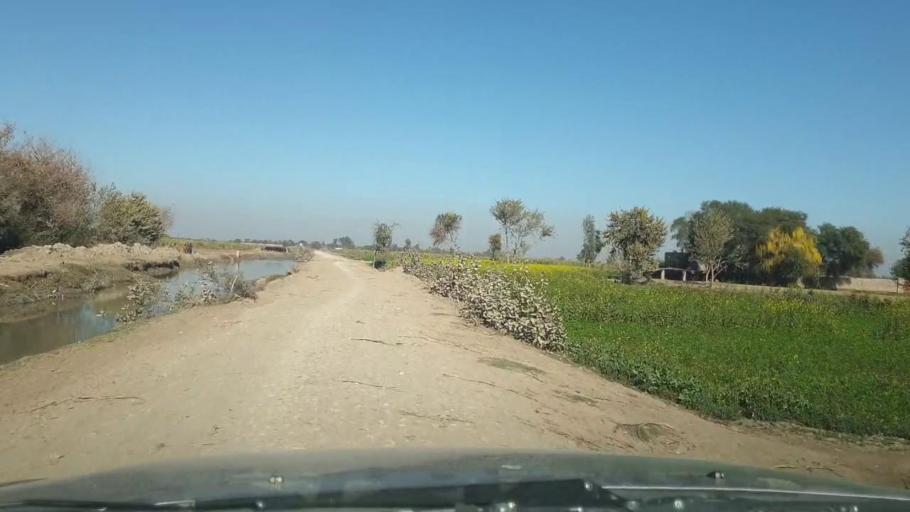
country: PK
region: Sindh
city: Ghotki
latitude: 28.0345
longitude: 69.2463
